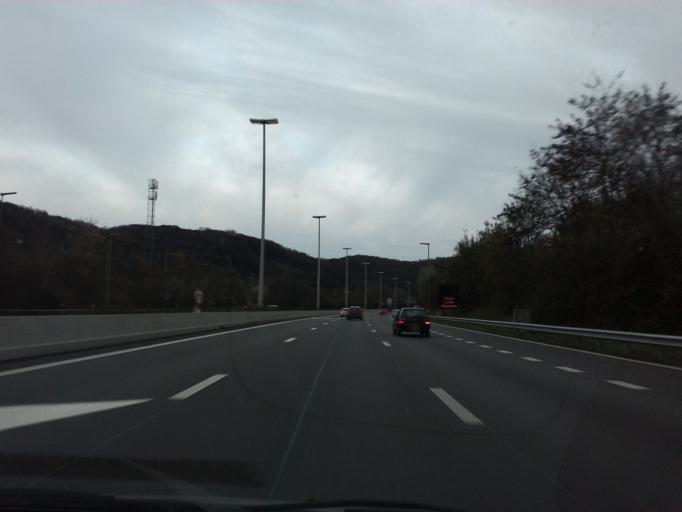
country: BE
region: Wallonia
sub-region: Province de Liege
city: Chaudfontaine
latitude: 50.5905
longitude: 5.5918
